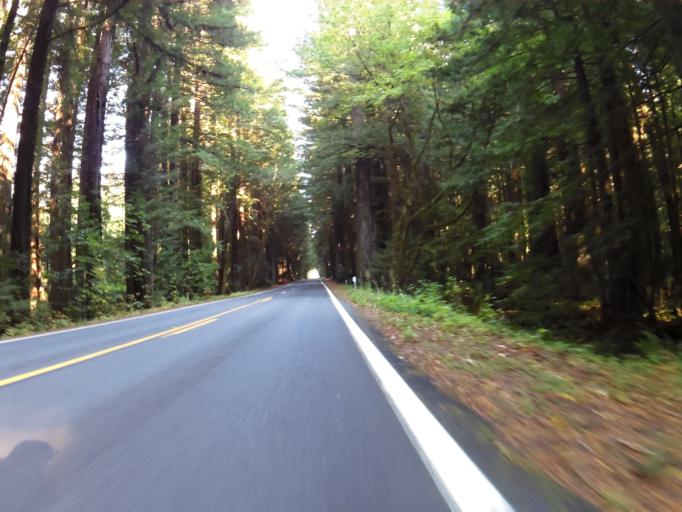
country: US
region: California
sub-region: Humboldt County
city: Rio Dell
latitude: 40.4460
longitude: -124.0082
